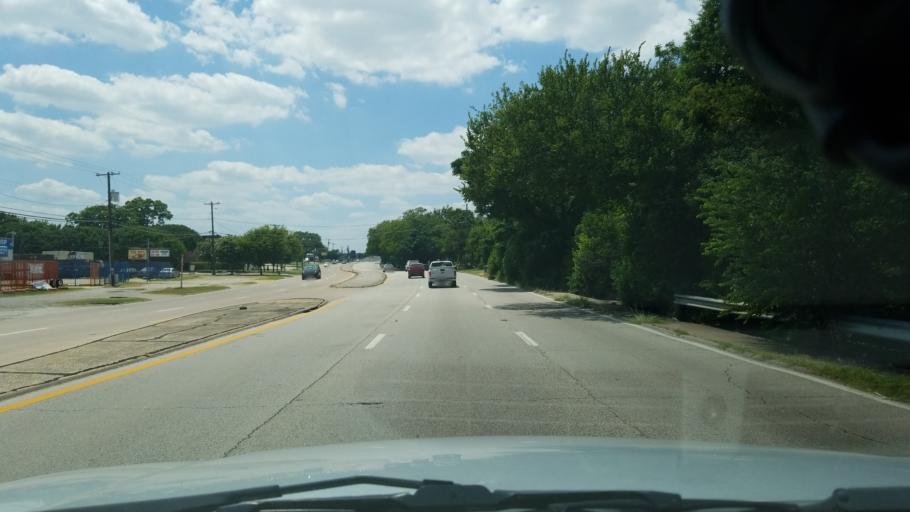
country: US
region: Texas
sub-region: Dallas County
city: Cockrell Hill
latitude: 32.6914
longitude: -96.8816
